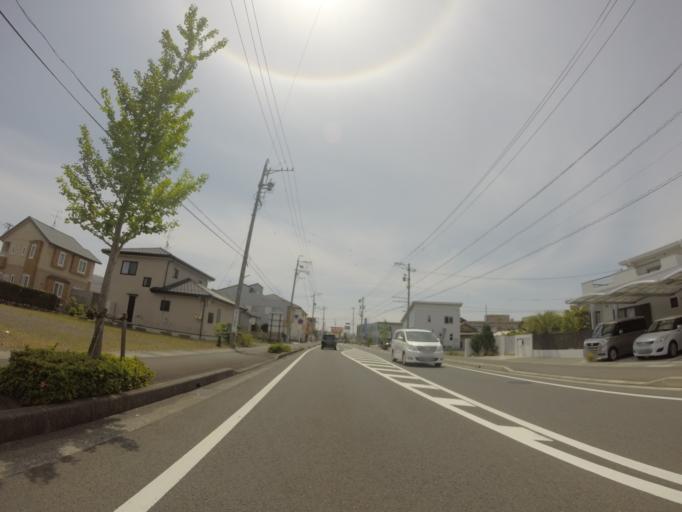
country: JP
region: Shizuoka
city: Yaizu
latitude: 34.8407
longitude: 138.3081
